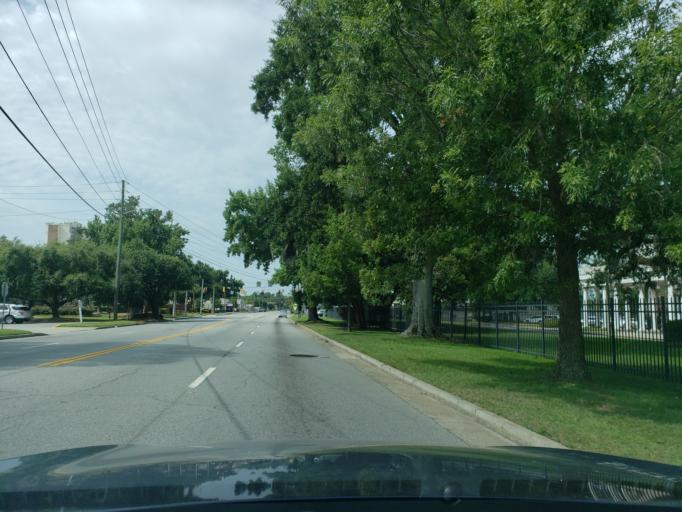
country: US
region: Georgia
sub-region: Chatham County
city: Thunderbolt
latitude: 32.0329
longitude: -81.0915
